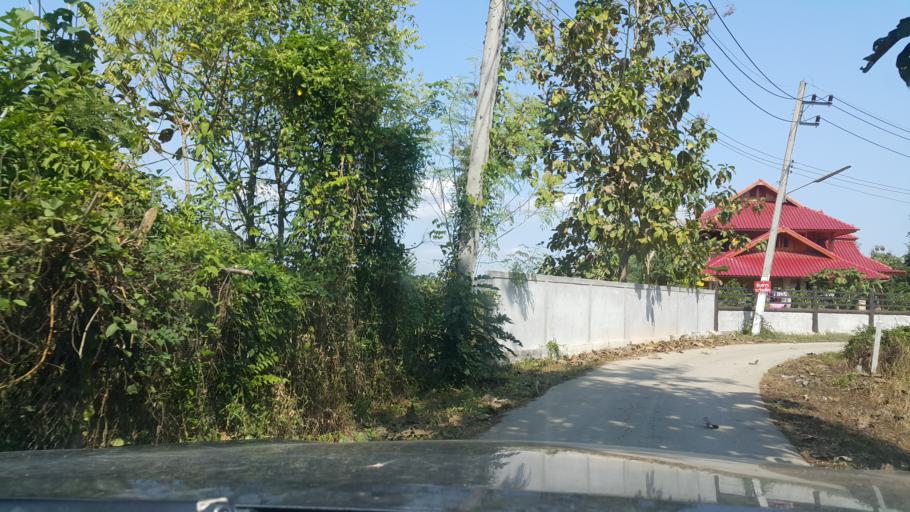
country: TH
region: Sukhothai
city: Thung Saliam
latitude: 17.3194
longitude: 99.5735
